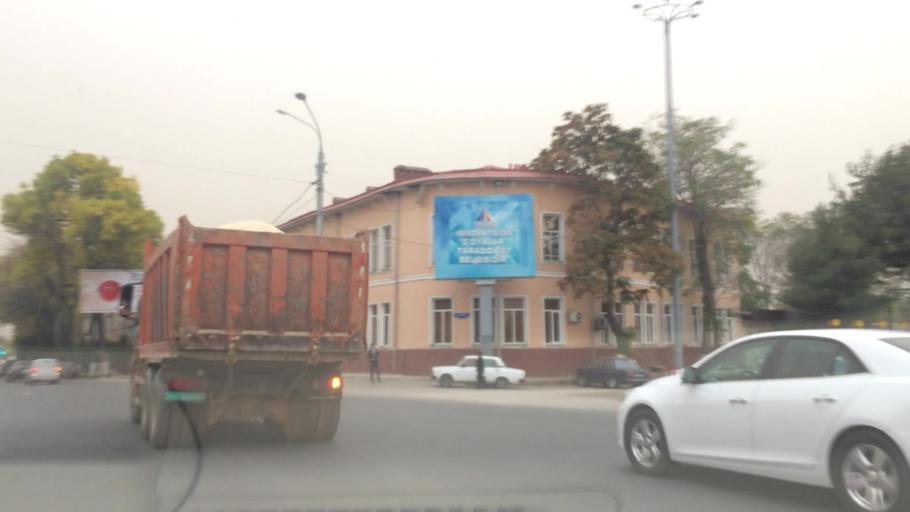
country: UZ
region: Toshkent Shahri
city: Tashkent
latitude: 41.3043
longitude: 69.2473
